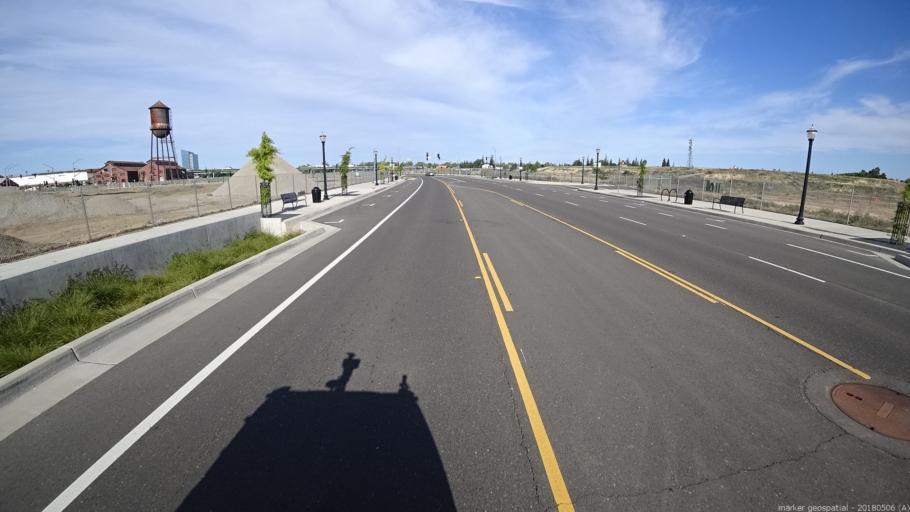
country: US
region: California
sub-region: Sacramento County
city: Sacramento
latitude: 38.5900
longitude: -121.4961
